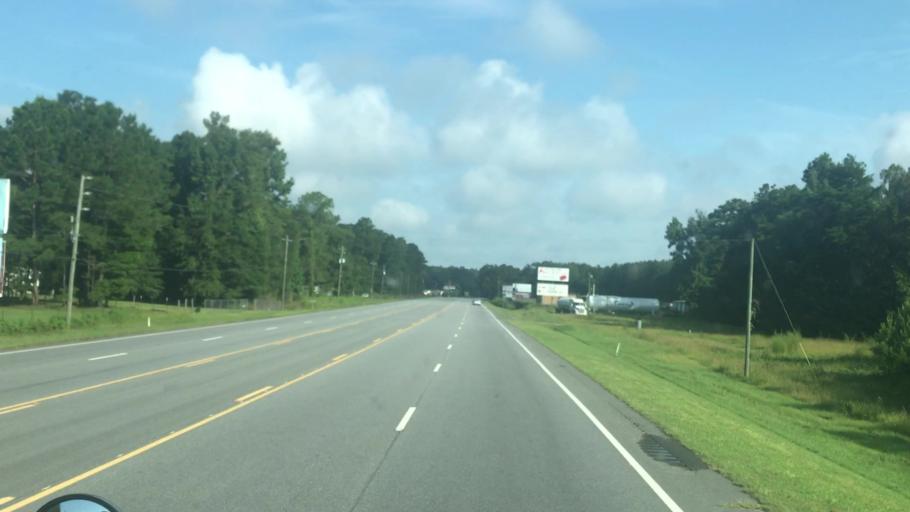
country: US
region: Georgia
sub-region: Decatur County
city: Bainbridge
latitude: 30.8665
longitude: -84.5562
